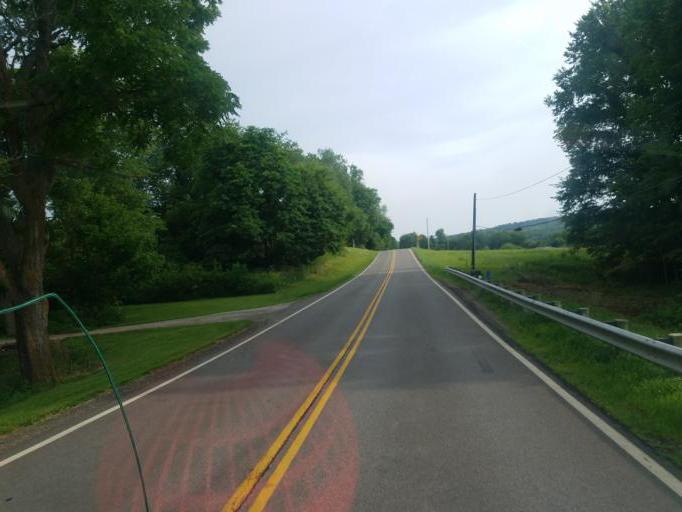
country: US
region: Ohio
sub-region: Ashland County
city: Loudonville
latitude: 40.7389
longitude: -82.2865
